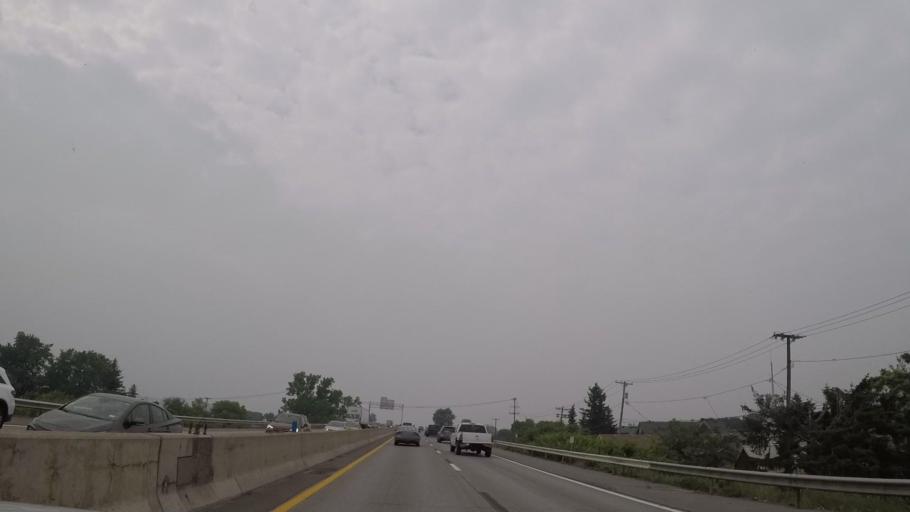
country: US
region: New York
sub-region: Erie County
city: Kenmore
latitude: 42.9414
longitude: -78.9068
